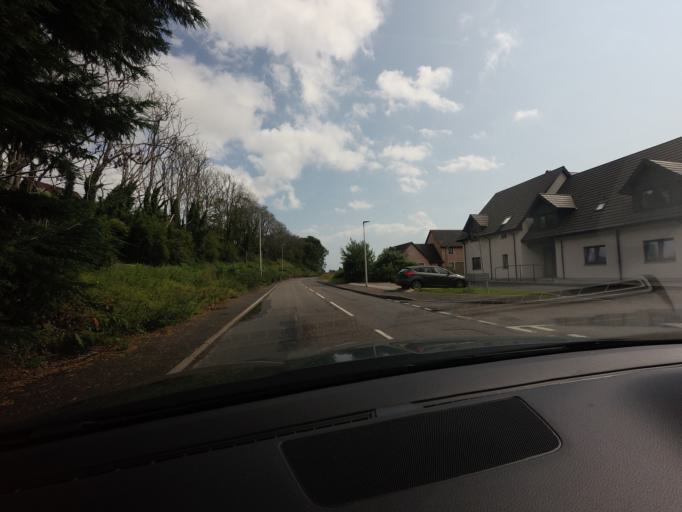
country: GB
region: Scotland
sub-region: Highland
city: Dingwall
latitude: 57.6030
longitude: -4.4237
